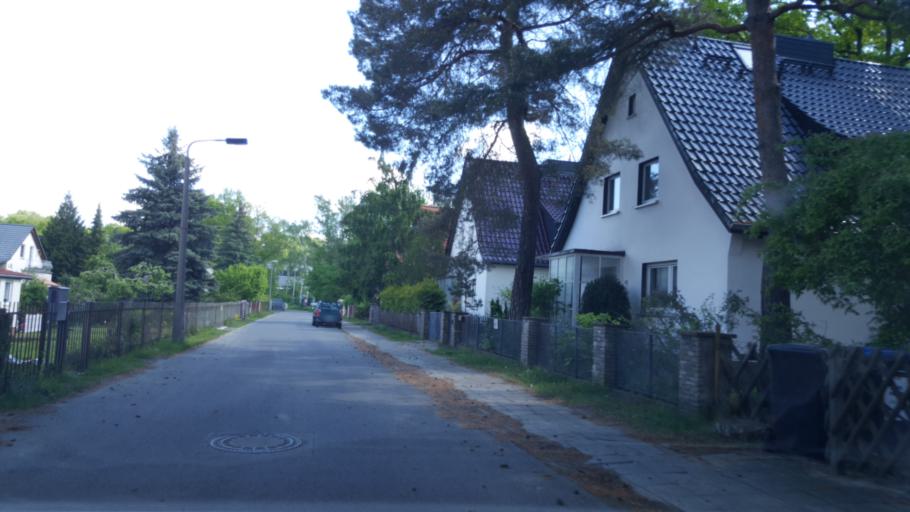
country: DE
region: Berlin
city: Berlin Koepenick
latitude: 52.4454
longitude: 13.5987
